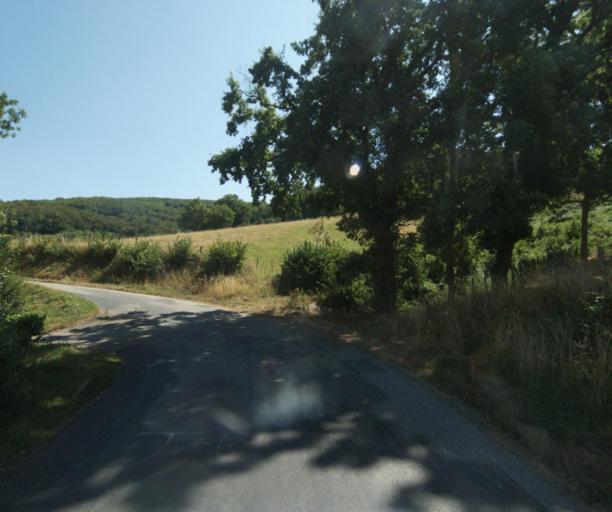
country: FR
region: Rhone-Alpes
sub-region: Departement du Rhone
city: Courzieu
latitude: 45.7288
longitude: 4.5559
